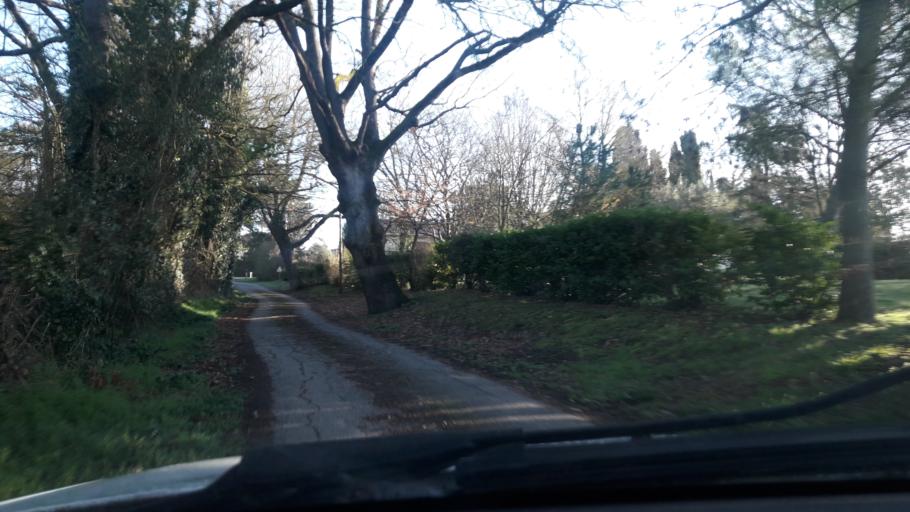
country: FR
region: Midi-Pyrenees
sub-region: Departement du Gers
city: Gimont
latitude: 43.6399
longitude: 0.9980
